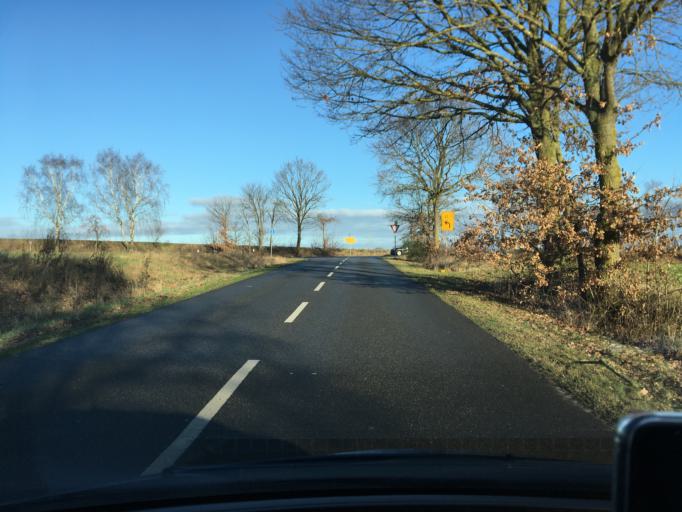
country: DE
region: Lower Saxony
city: Wendisch Evern
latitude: 53.2196
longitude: 10.4776
